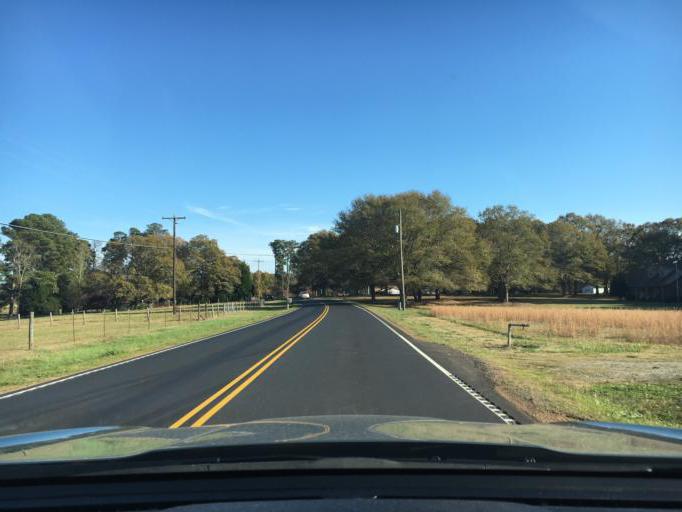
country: US
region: South Carolina
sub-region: Spartanburg County
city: Inman Mills
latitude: 35.0260
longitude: -82.0936
